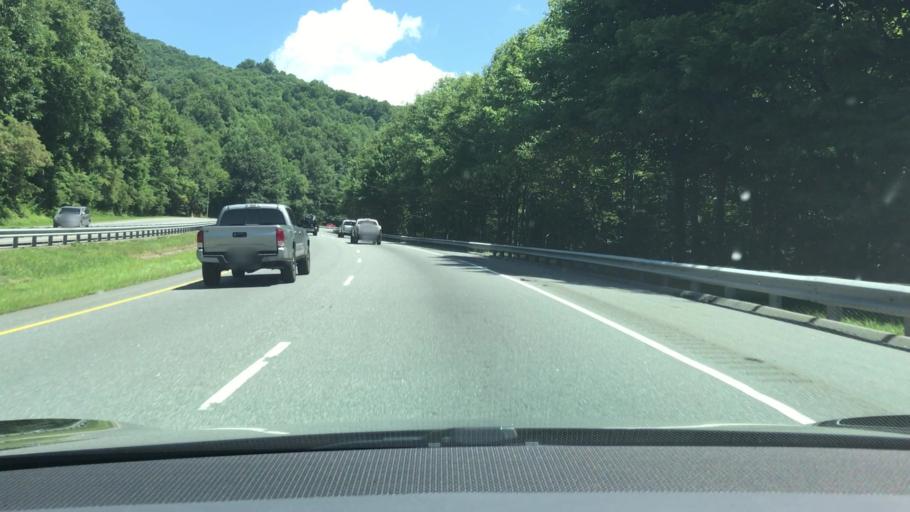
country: US
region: North Carolina
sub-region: Haywood County
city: Maggie Valley
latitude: 35.4300
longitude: -83.0970
